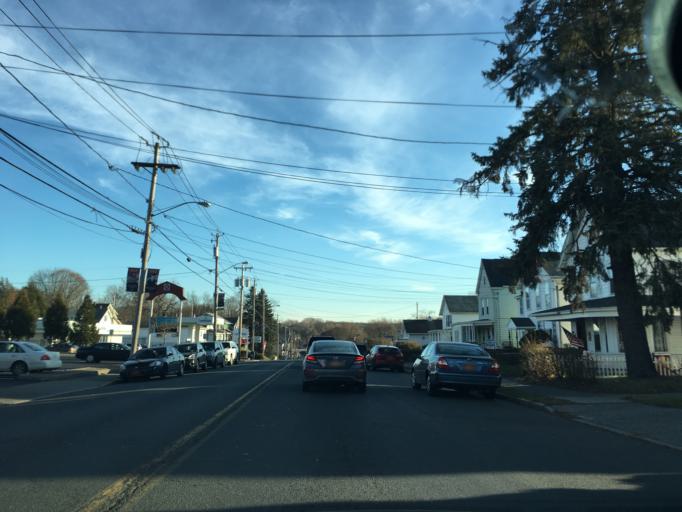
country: US
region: New York
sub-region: Rensselaer County
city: Wynantskill
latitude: 42.7048
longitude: -73.6595
